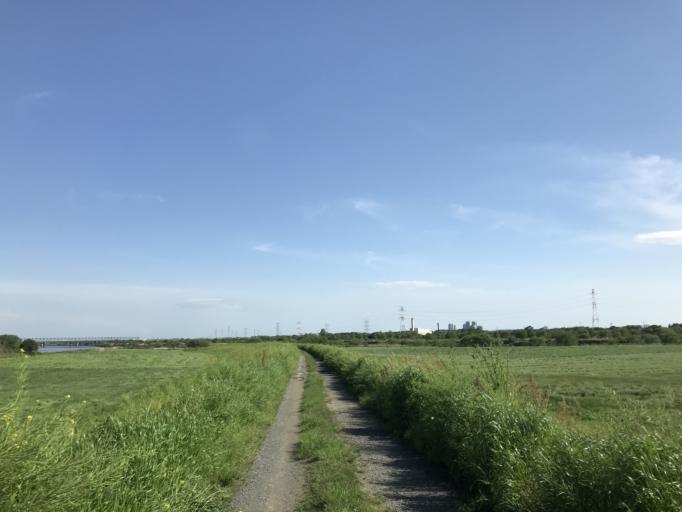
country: JP
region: Ibaraki
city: Moriya
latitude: 35.9432
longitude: 139.9436
